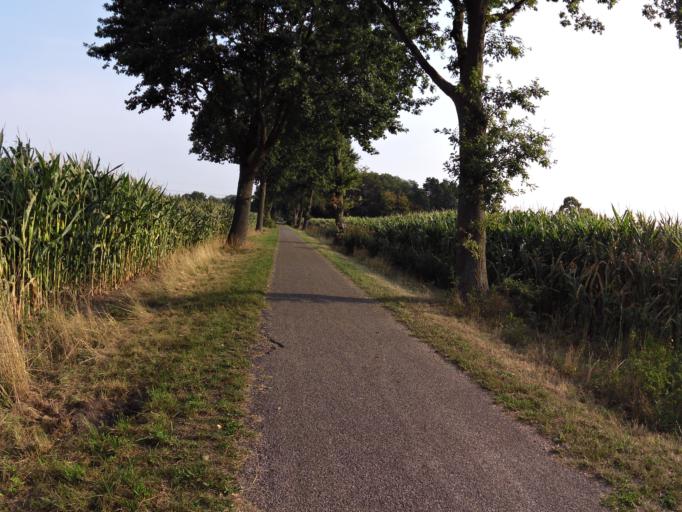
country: DE
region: North Rhine-Westphalia
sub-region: Regierungsbezirk Detmold
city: Petershagen
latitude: 52.4042
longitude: 8.9651
